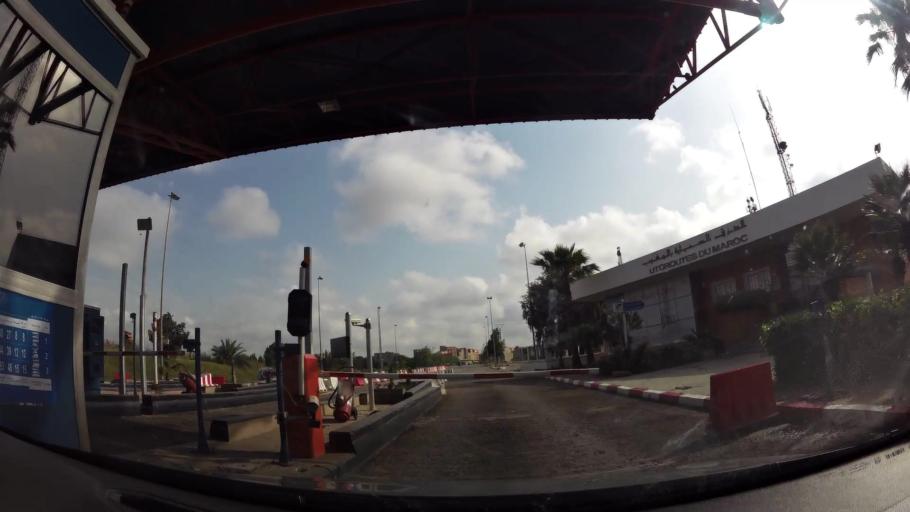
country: MA
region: Rabat-Sale-Zemmour-Zaer
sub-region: Khemisset
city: Tiflet
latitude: 33.8813
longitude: -6.3224
